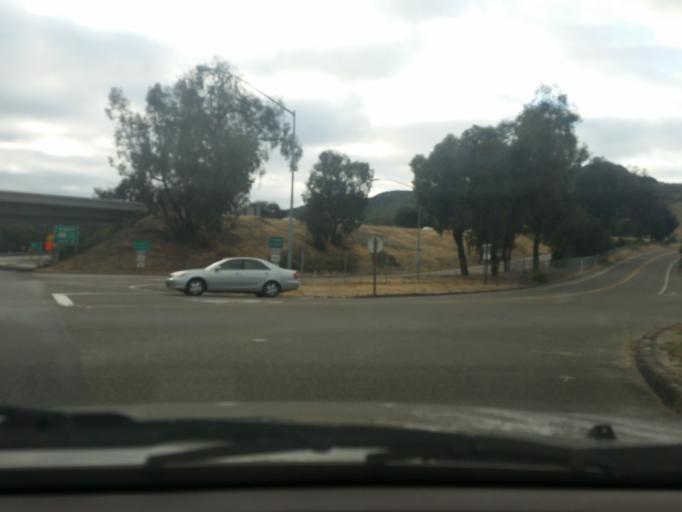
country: US
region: California
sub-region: San Luis Obispo County
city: Avila Beach
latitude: 35.1797
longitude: -120.7005
